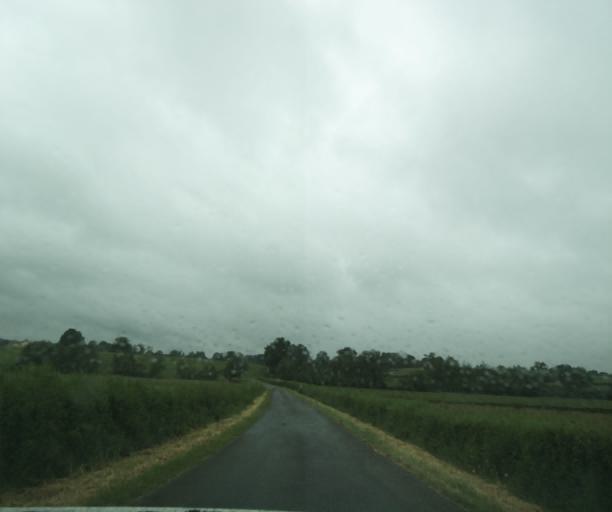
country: FR
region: Bourgogne
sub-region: Departement de Saone-et-Loire
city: Palinges
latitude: 46.4899
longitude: 4.1954
